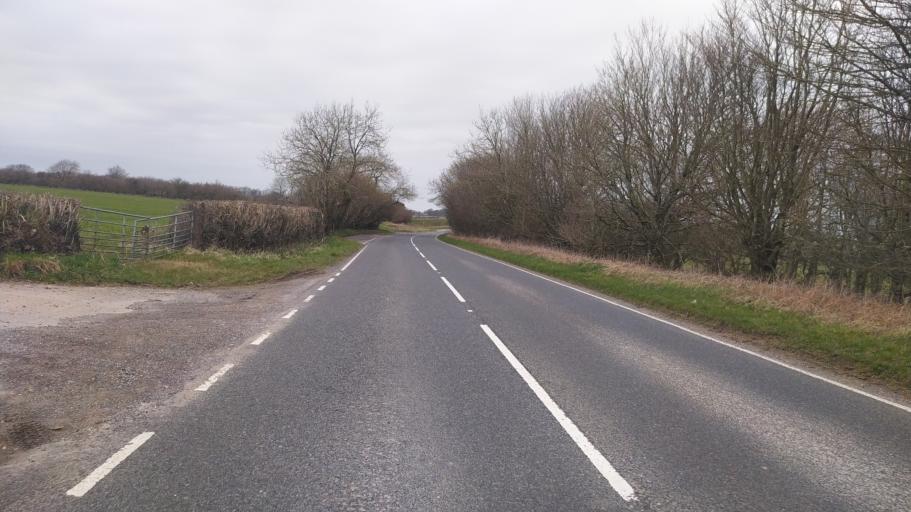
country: GB
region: England
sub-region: Dorset
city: Beaminster
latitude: 50.8275
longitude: -2.6836
